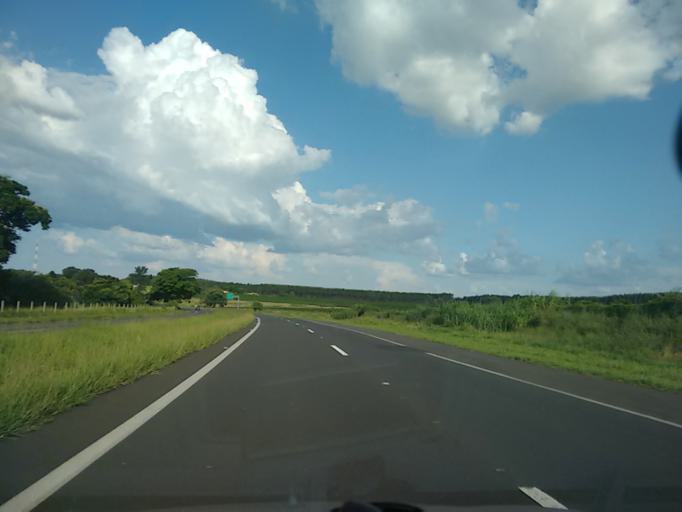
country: BR
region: Sao Paulo
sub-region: Duartina
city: Duartina
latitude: -22.3305
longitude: -49.4594
